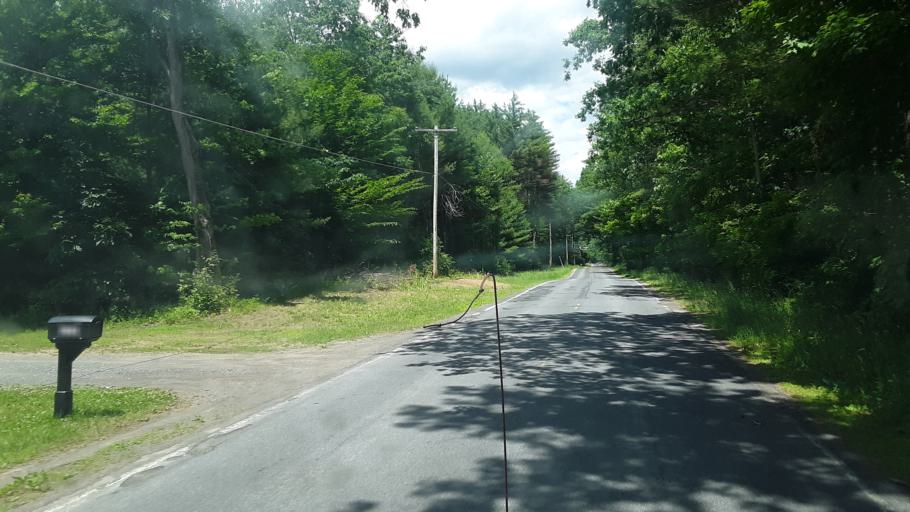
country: US
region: New York
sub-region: Oneida County
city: Rome
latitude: 43.2464
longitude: -75.5971
